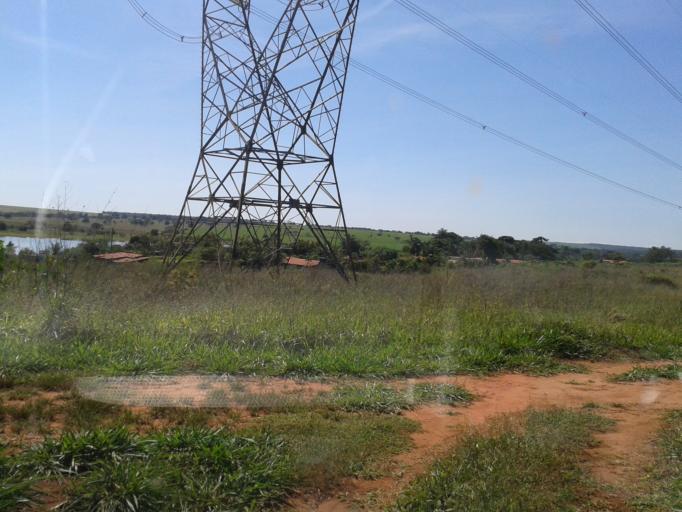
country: BR
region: Minas Gerais
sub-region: Santa Vitoria
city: Santa Vitoria
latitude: -19.0083
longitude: -50.3263
